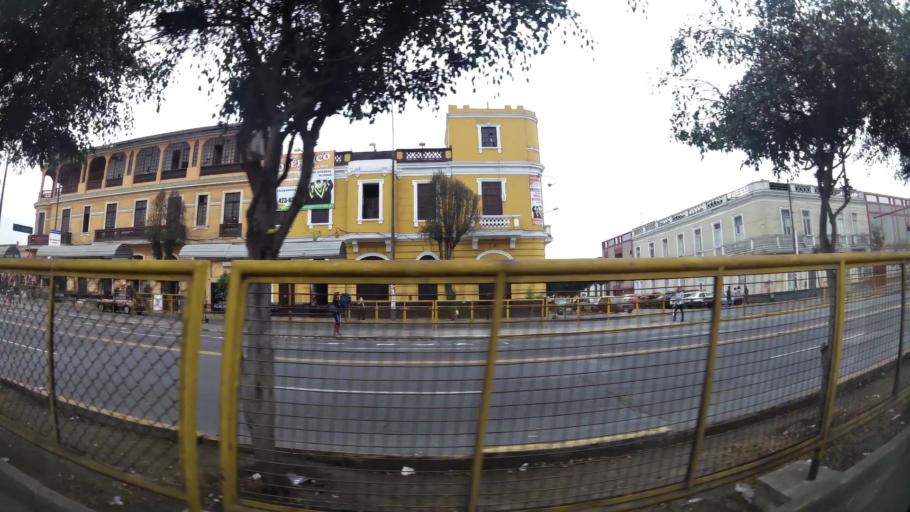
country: PE
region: Lima
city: Lima
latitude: -12.0611
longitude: -77.0423
